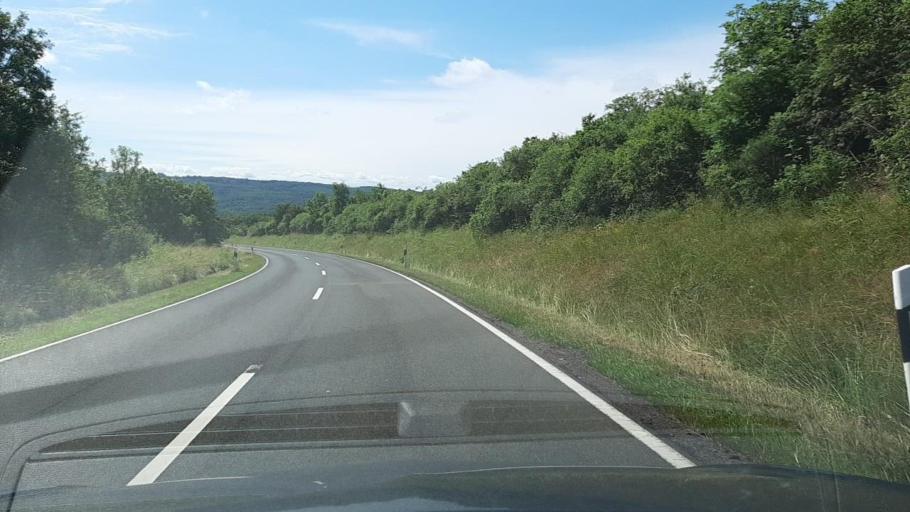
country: DE
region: Rheinland-Pfalz
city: Mesenich
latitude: 50.0998
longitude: 7.1789
